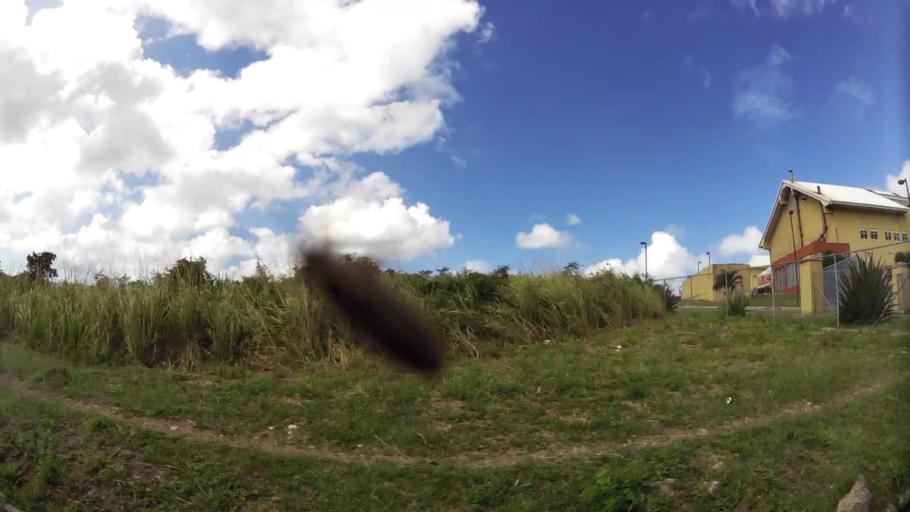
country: AG
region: Saint John
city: Saint John's
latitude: 17.1156
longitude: -61.8384
